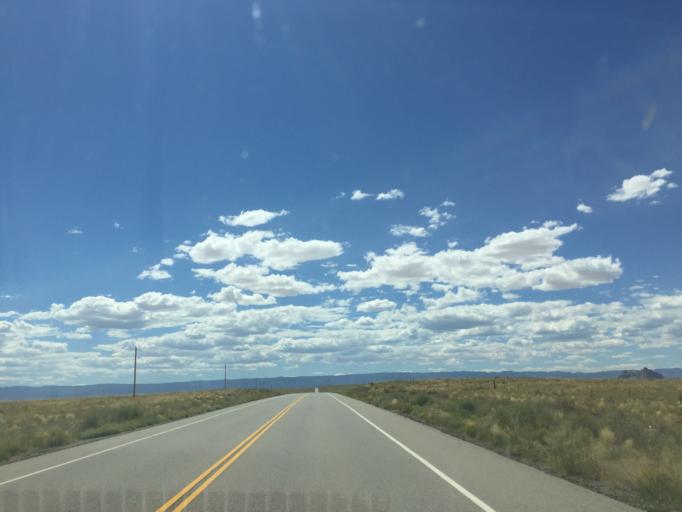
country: US
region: New Mexico
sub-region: San Juan County
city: Waterflow
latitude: 36.3635
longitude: -108.5880
